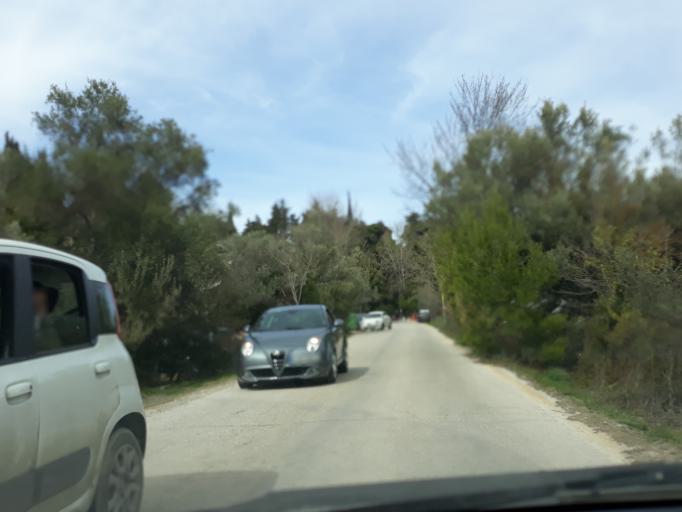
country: GR
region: Attica
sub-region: Nomarchia Anatolikis Attikis
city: Varybobi
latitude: 38.1595
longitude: 23.7920
